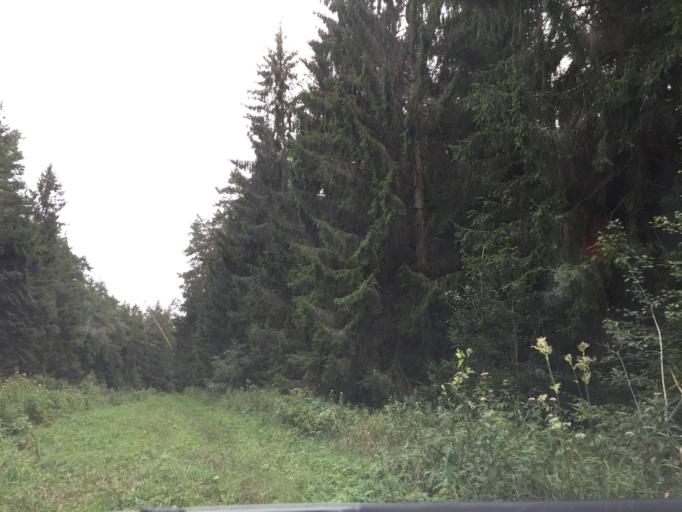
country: LV
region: Jaunpils
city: Jaunpils
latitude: 56.7308
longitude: 23.0876
